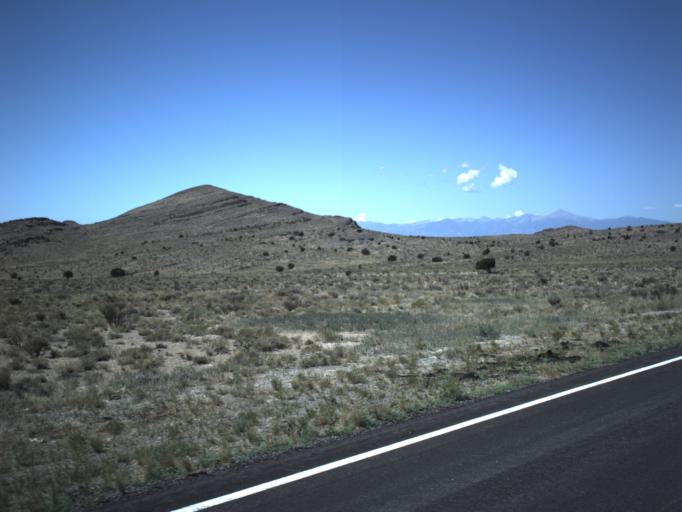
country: US
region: Utah
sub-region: Beaver County
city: Milford
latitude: 39.0774
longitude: -113.6893
